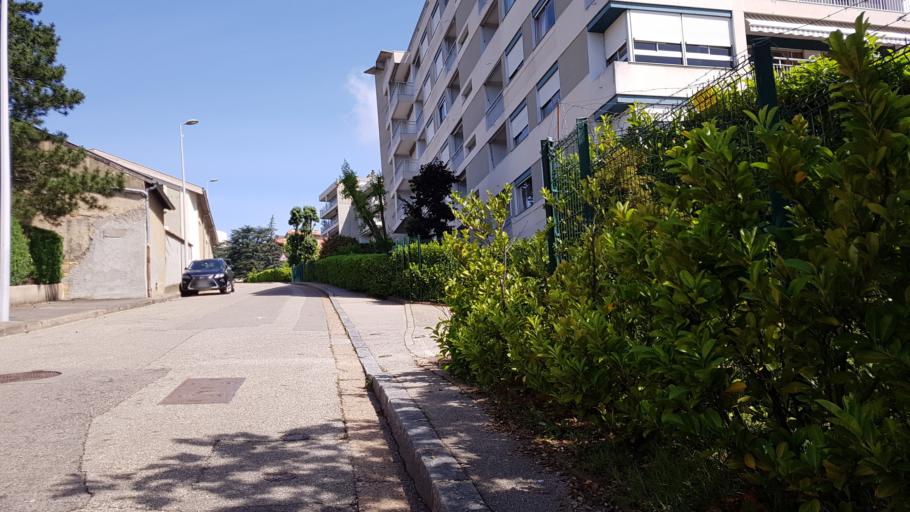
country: FR
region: Rhone-Alpes
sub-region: Departement du Rhone
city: Caluire-et-Cuire
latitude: 45.7907
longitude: 4.8545
